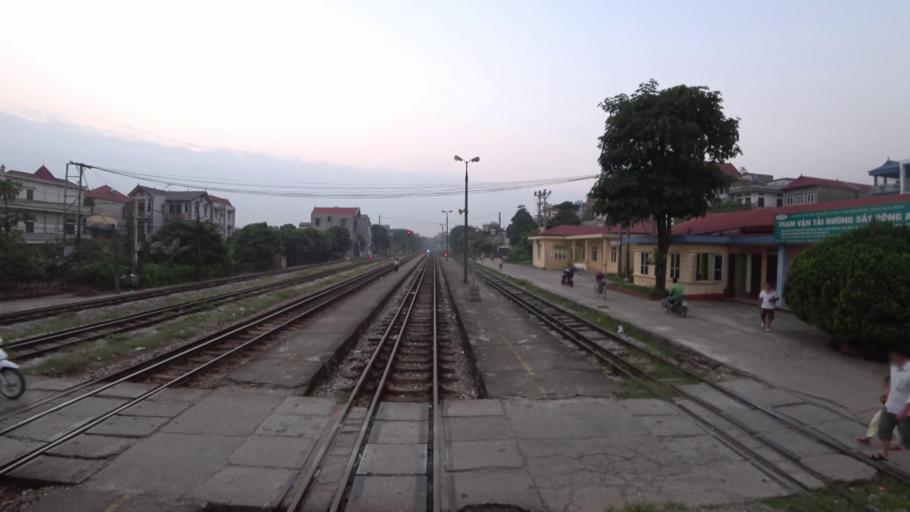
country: VN
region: Ha Noi
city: Soc Son
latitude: 21.2122
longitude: 105.8576
